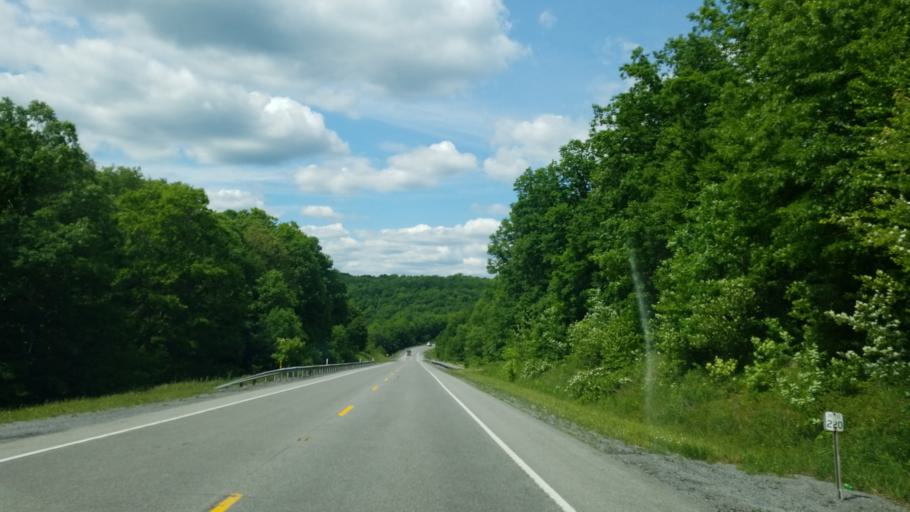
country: US
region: Pennsylvania
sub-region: Clearfield County
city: Clearfield
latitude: 40.9503
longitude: -78.3745
